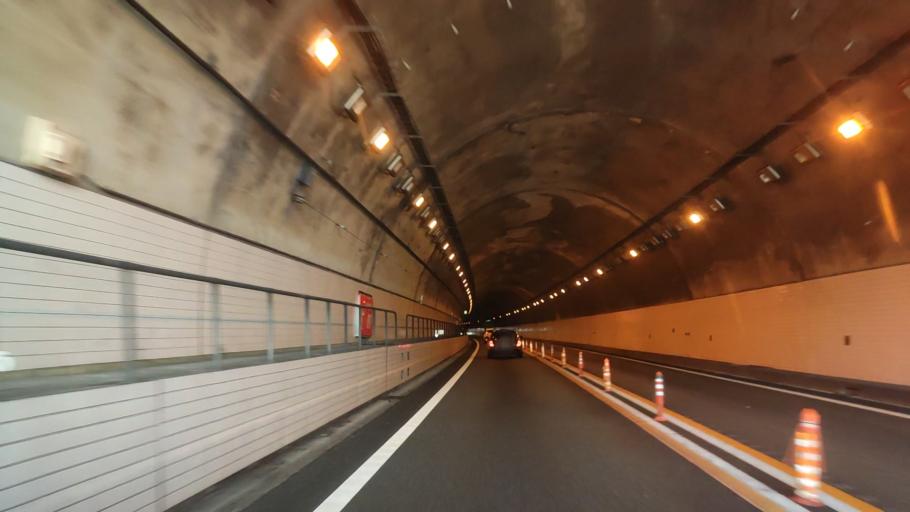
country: JP
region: Tokushima
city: Ikedacho
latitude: 34.0253
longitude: 133.7814
